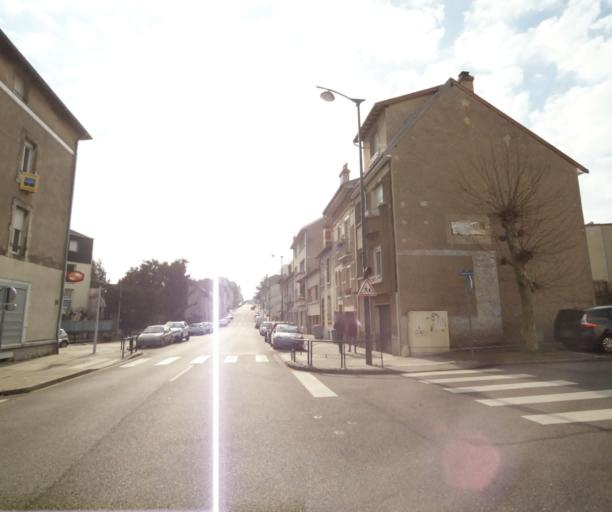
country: FR
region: Lorraine
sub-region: Departement de Meurthe-et-Moselle
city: Laxou
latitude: 48.6822
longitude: 6.1559
